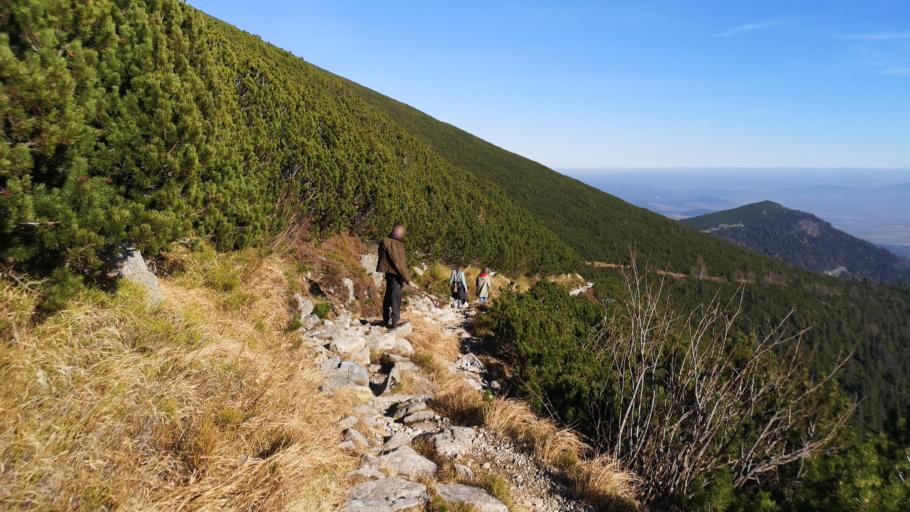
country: SK
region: Presovsky
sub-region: Okres Poprad
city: Vysoke Tatry
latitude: 49.1994
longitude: 20.2420
